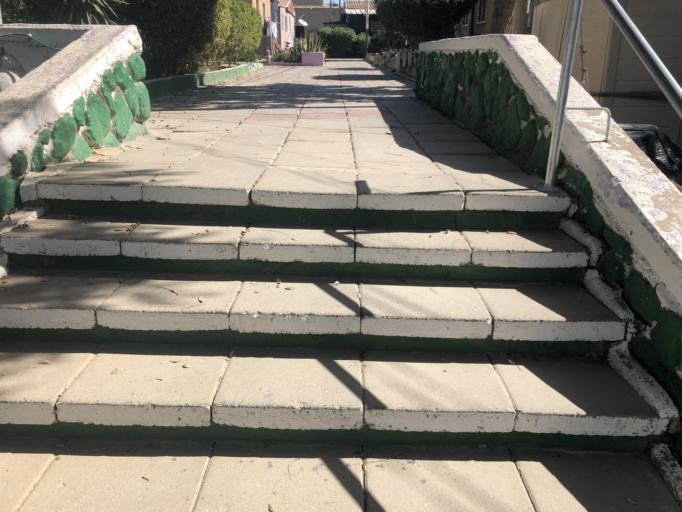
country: IL
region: Southern District
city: Dimona
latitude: 31.0672
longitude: 35.0407
